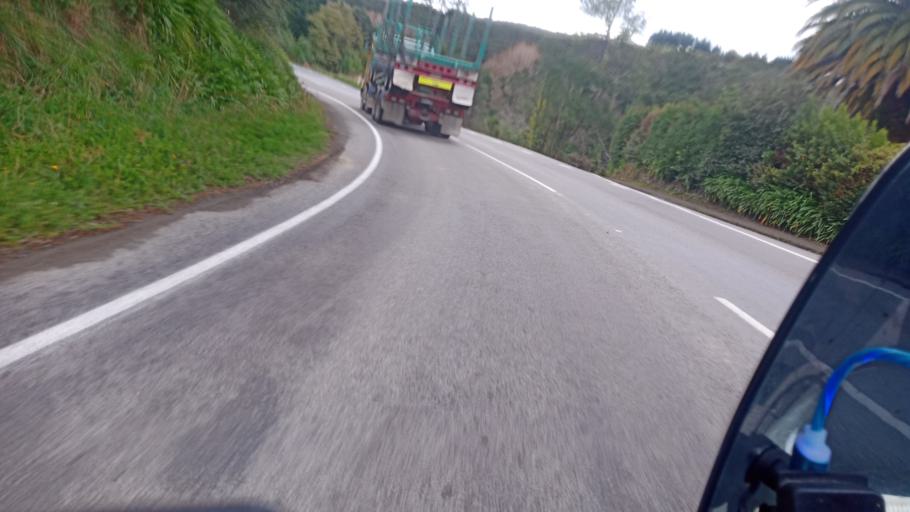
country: NZ
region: Gisborne
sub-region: Gisborne District
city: Gisborne
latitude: -38.0537
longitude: 178.3092
